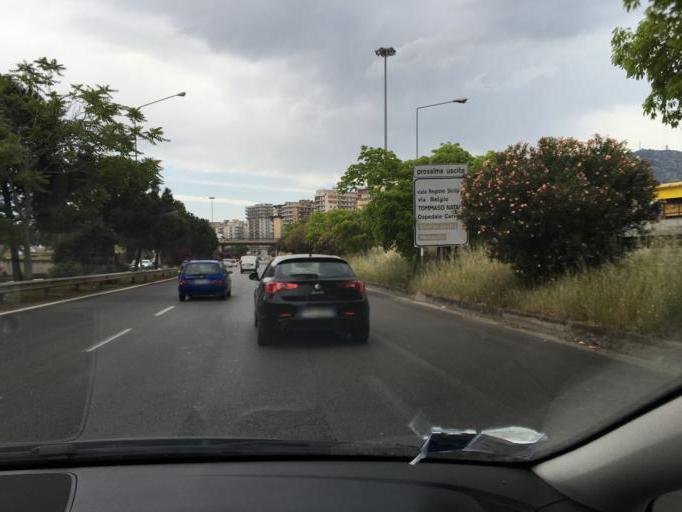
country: IT
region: Sicily
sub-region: Palermo
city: Palermo
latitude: 38.1377
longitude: 13.3310
